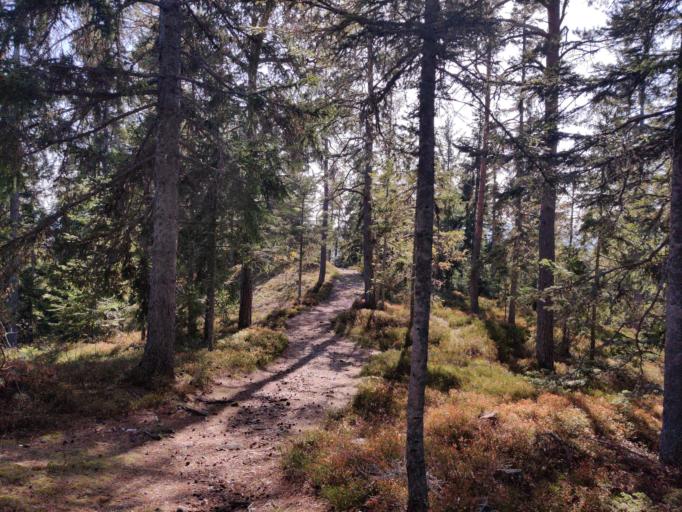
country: AT
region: Styria
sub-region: Politischer Bezirk Hartberg-Fuerstenfeld
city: Sankt Jakob im Walde
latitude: 47.4666
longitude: 15.8175
